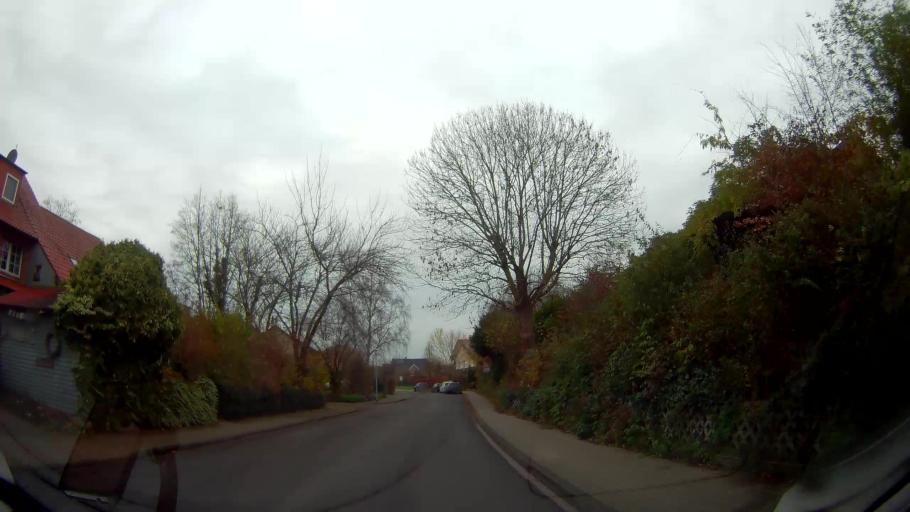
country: DE
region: North Rhine-Westphalia
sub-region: Regierungsbezirk Munster
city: Haltern
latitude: 51.7509
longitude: 7.1872
